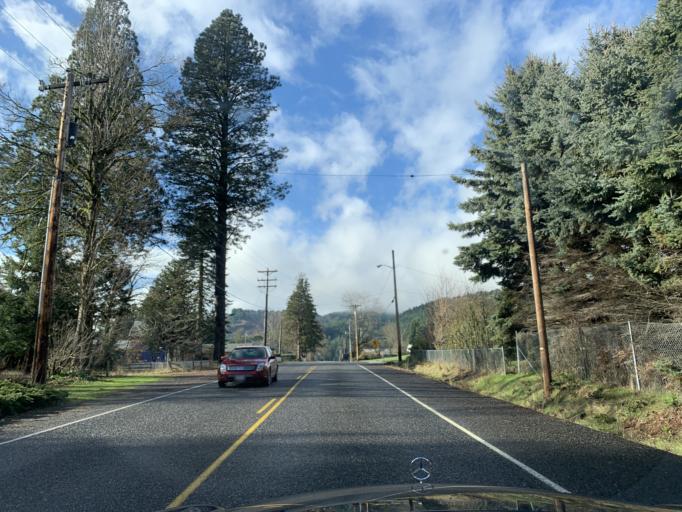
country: US
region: Washington
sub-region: Skamania County
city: Carson
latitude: 45.7261
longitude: -121.8091
